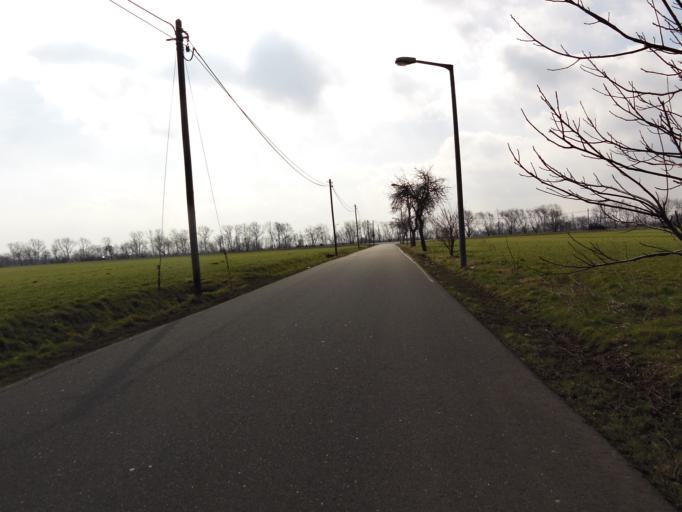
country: DE
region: Saxony
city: Markranstadt
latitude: 51.3036
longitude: 12.2934
